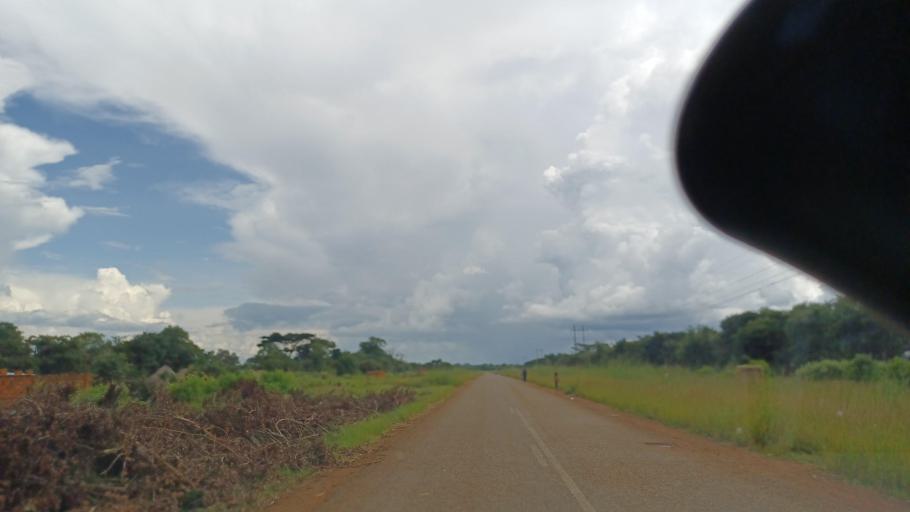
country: ZM
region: North-Western
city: Kasempa
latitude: -13.1142
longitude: 25.8697
